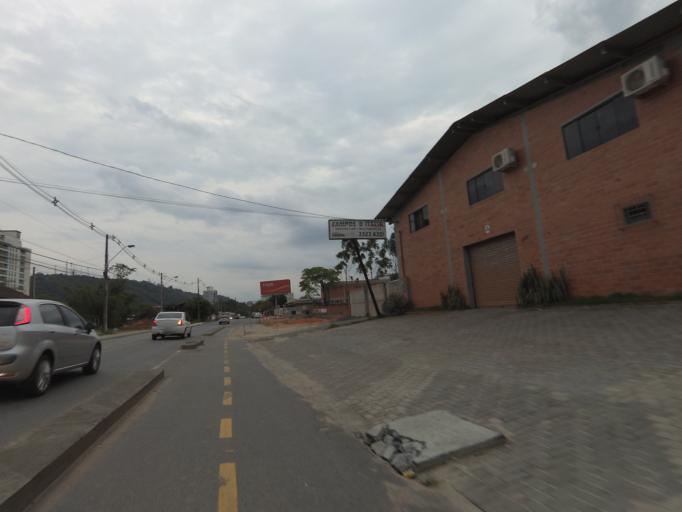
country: BR
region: Santa Catarina
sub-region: Blumenau
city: Blumenau
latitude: -26.8903
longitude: -49.0632
